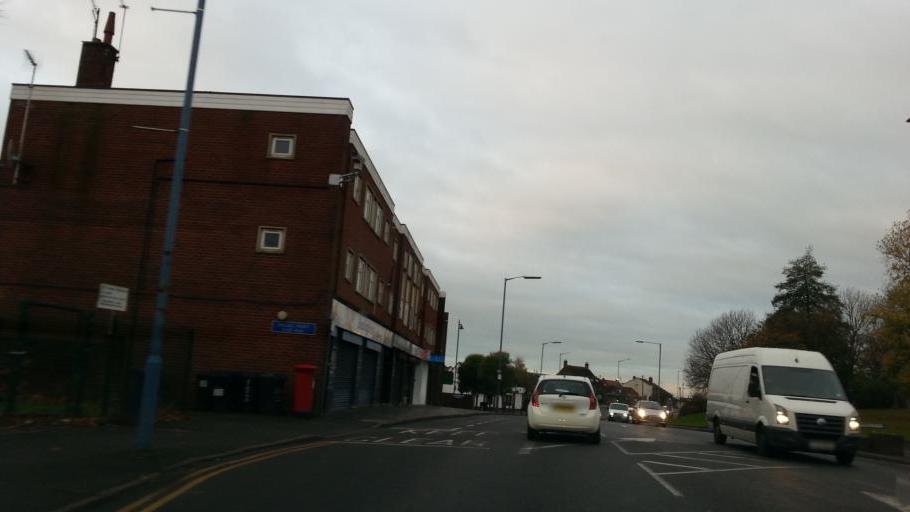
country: GB
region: England
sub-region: Sandwell
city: Wednesbury
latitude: 52.5535
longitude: -2.0173
